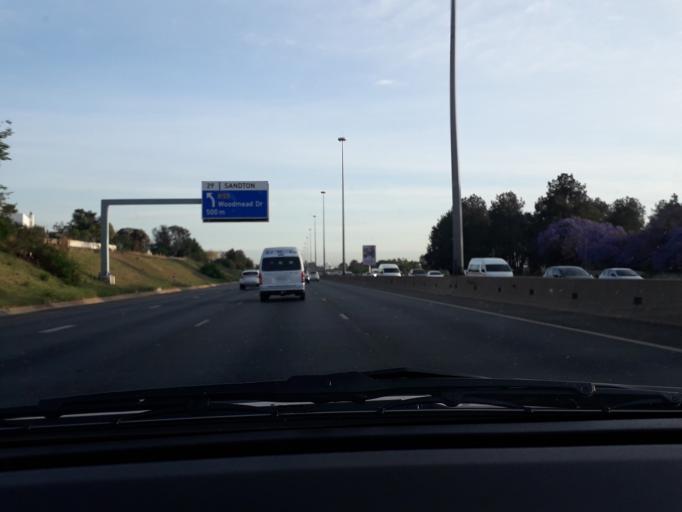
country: ZA
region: Gauteng
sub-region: City of Johannesburg Metropolitan Municipality
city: Modderfontein
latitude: -26.0718
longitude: 28.0889
